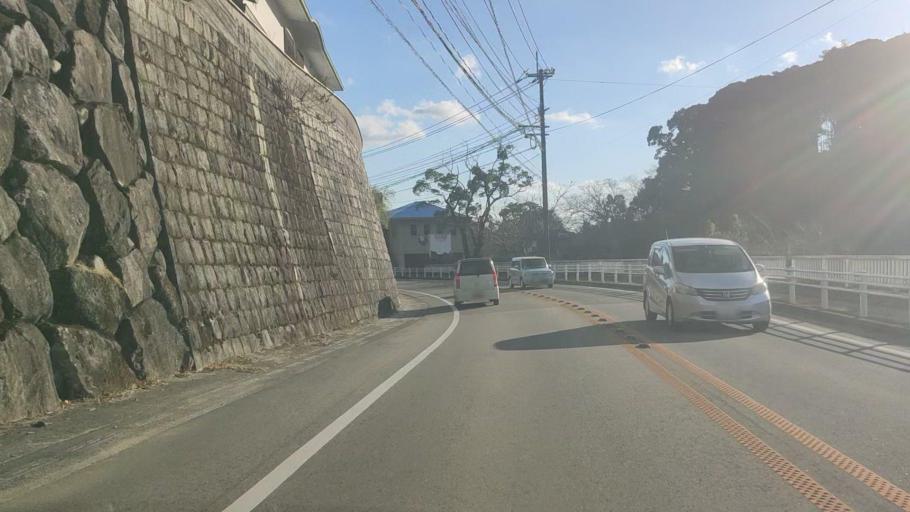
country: JP
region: Saga Prefecture
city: Saga-shi
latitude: 33.3296
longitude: 130.2685
